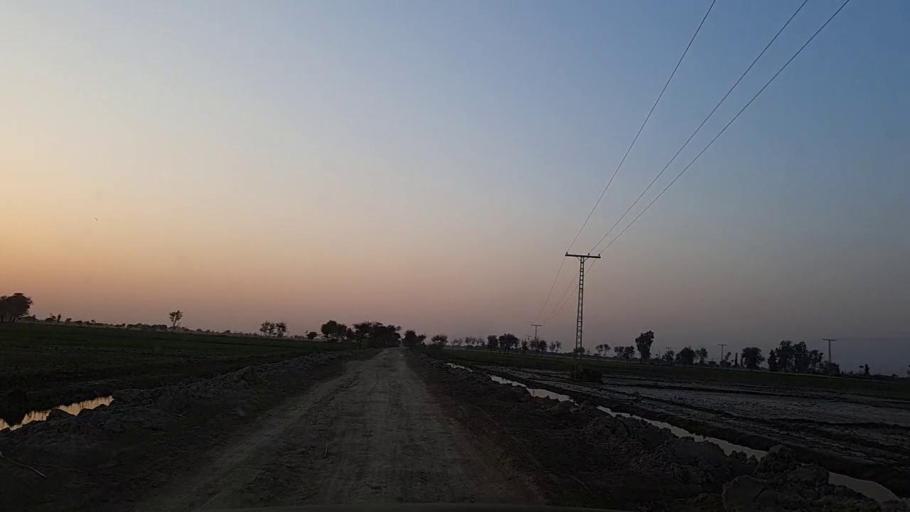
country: PK
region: Sindh
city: Bhit Shah
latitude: 25.9306
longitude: 68.4751
